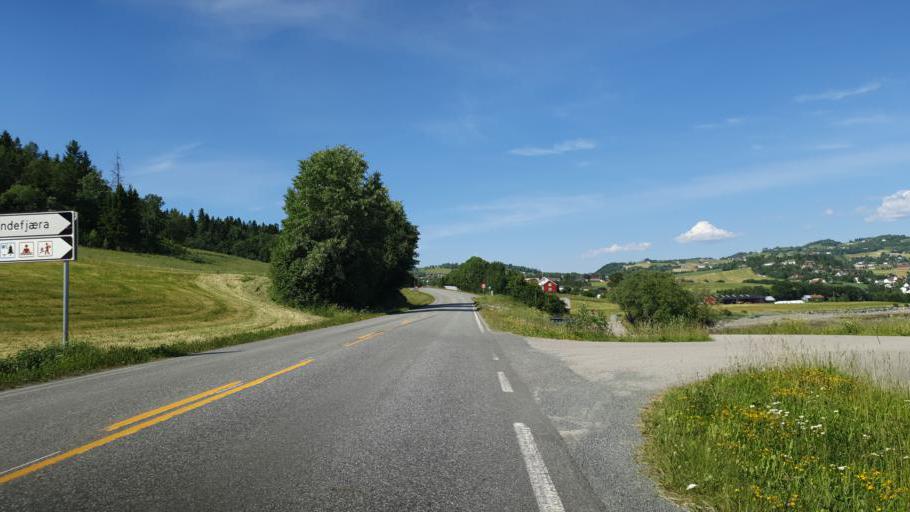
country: NO
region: Nord-Trondelag
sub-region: Leksvik
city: Leksvik
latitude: 63.6620
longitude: 10.6081
